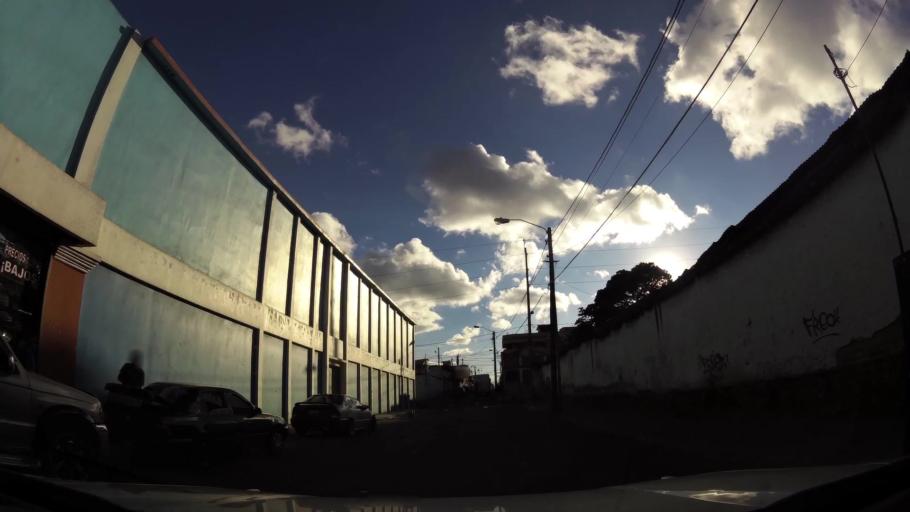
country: GT
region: Guatemala
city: Guatemala City
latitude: 14.6195
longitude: -90.5239
